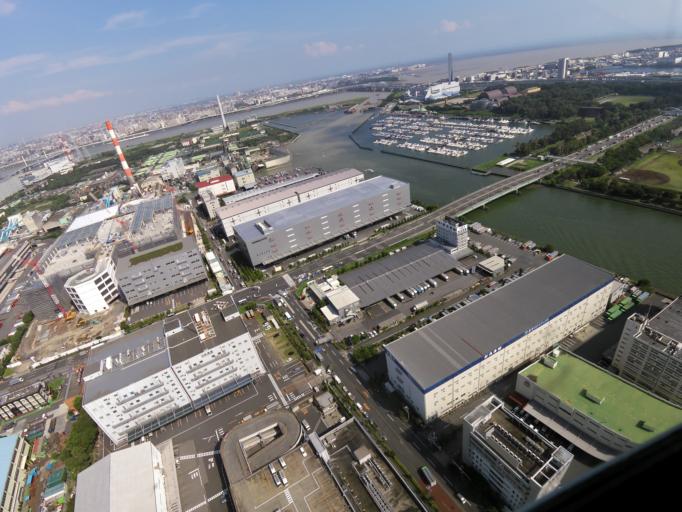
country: JP
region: Tokyo
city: Urayasu
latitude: 35.6579
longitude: 139.8210
